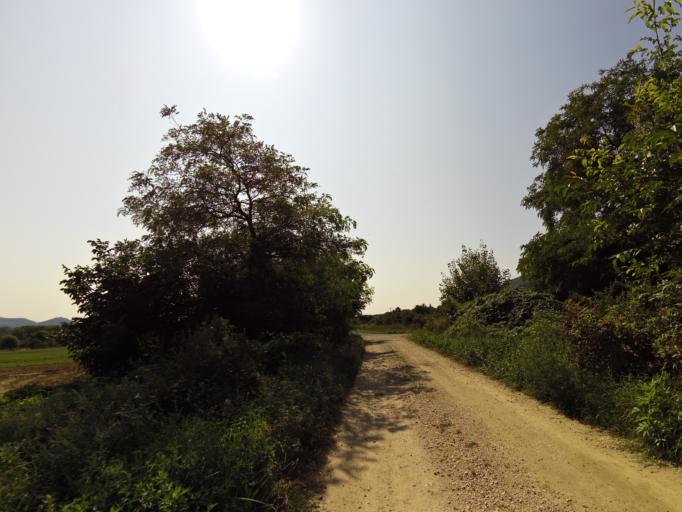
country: HU
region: Veszprem
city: Tapolca
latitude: 46.8304
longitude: 17.3679
